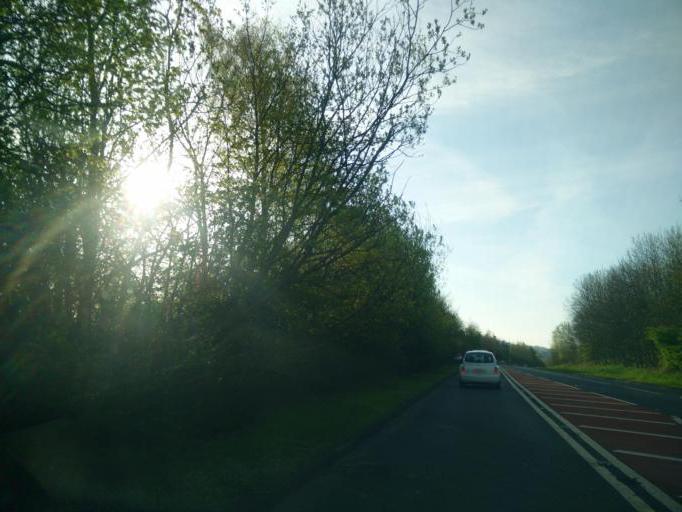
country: GB
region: England
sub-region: County Durham
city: Bishop Auckland
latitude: 54.6713
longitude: -1.6878
